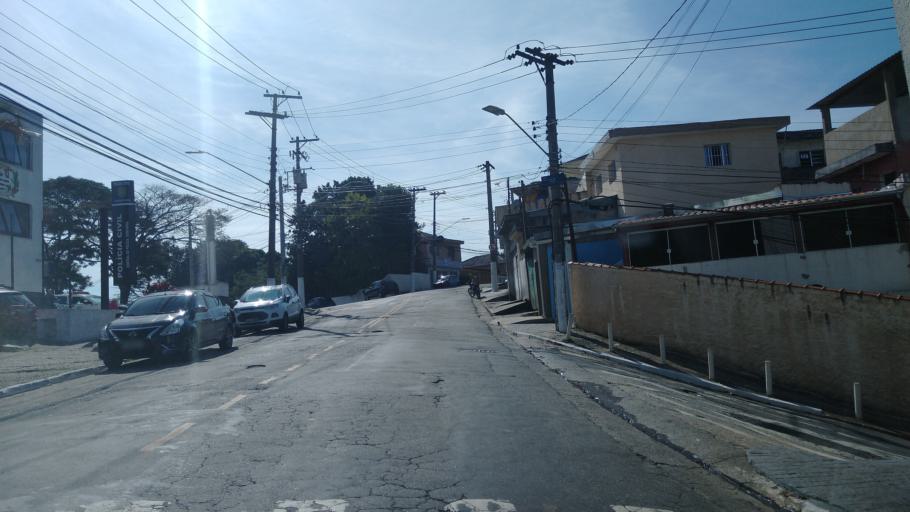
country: BR
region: Sao Paulo
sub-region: Sao Paulo
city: Sao Paulo
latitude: -23.4639
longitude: -46.6788
